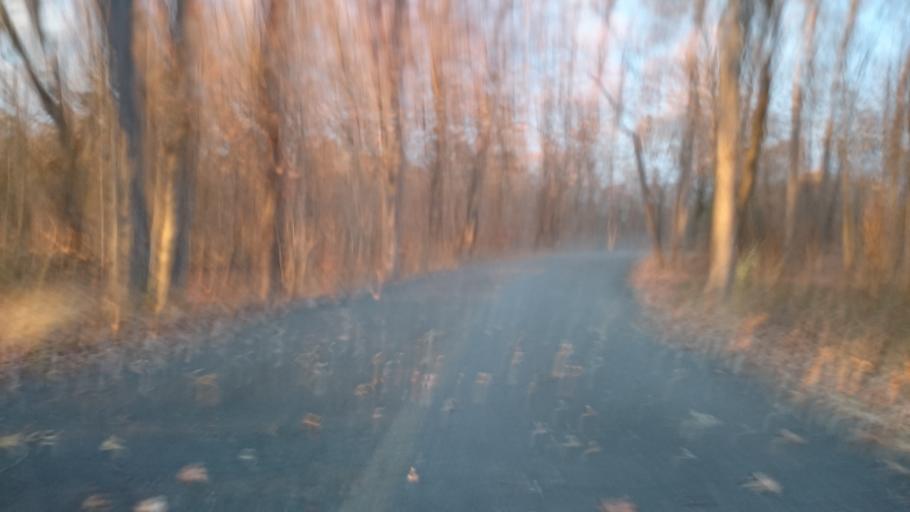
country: US
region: Connecticut
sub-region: New Haven County
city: New Haven
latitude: 41.3352
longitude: -72.9648
